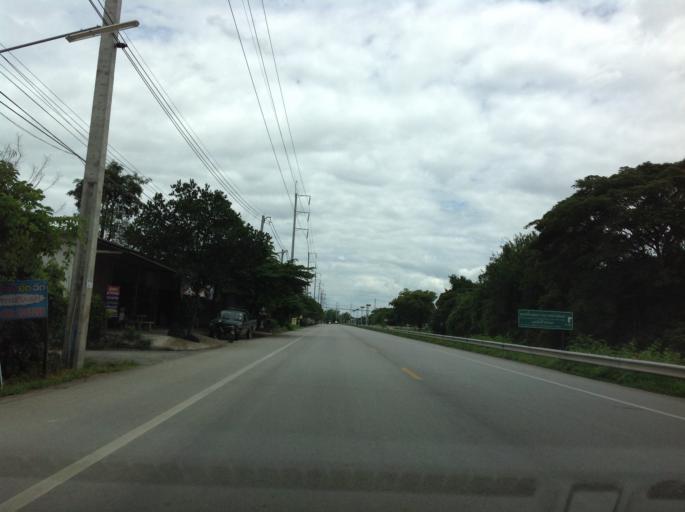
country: TH
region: Chiang Mai
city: Hang Dong
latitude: 18.6874
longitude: 98.8972
